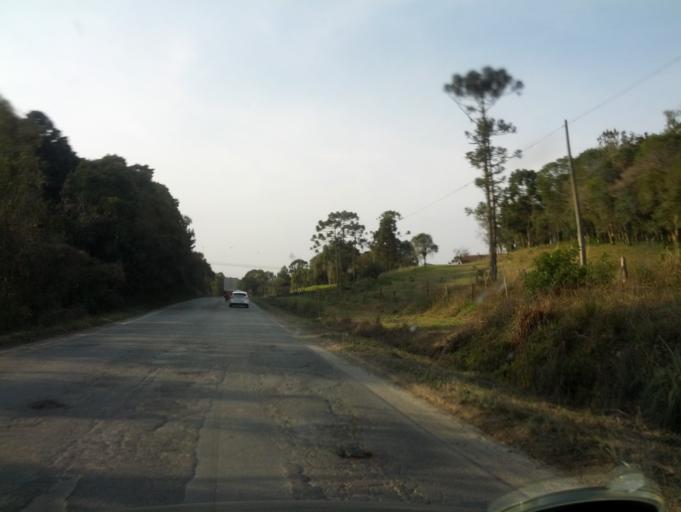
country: BR
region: Santa Catarina
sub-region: Otacilio Costa
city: Otacilio Costa
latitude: -27.5608
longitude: -50.1498
